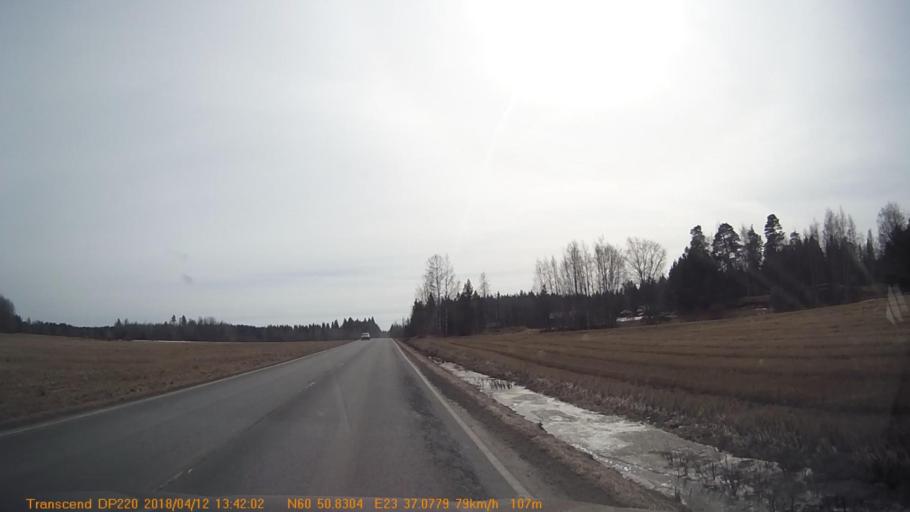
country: FI
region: Haeme
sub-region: Forssa
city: Forssa
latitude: 60.8465
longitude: 23.6180
